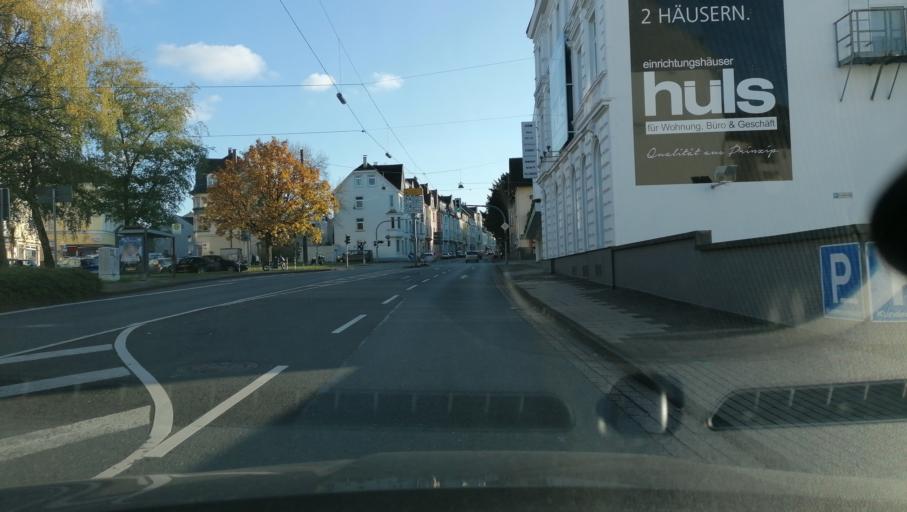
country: DE
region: North Rhine-Westphalia
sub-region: Regierungsbezirk Arnsberg
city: Schwelm
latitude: 51.2891
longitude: 7.2894
